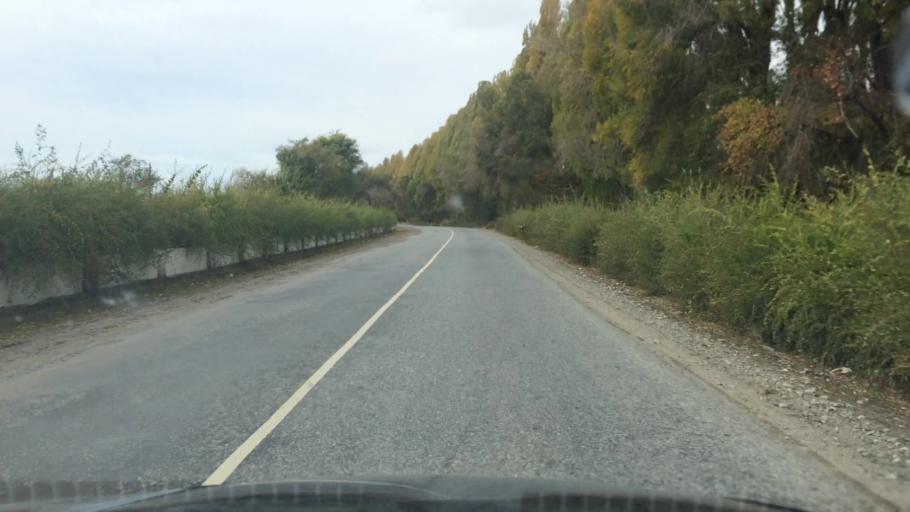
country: KG
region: Ysyk-Koel
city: Pokrovka
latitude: 42.7396
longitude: 77.9037
